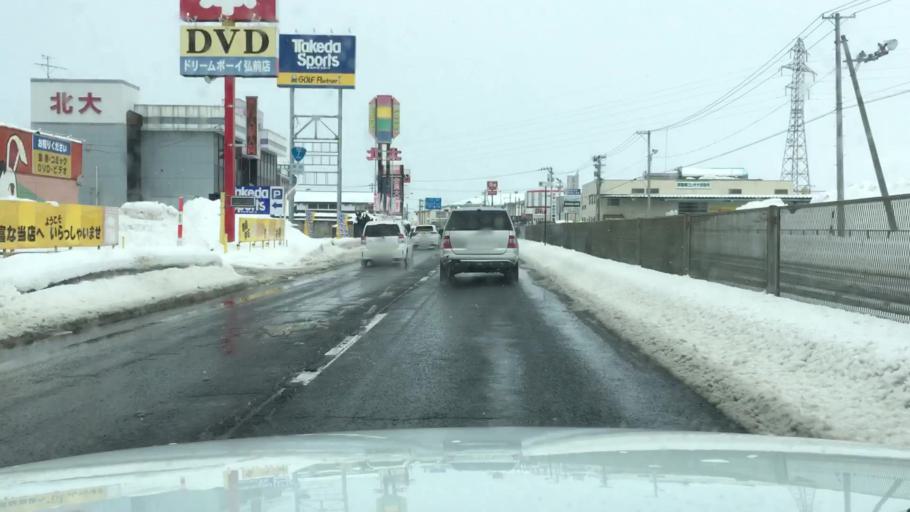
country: JP
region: Aomori
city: Hirosaki
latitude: 40.6081
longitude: 140.4989
